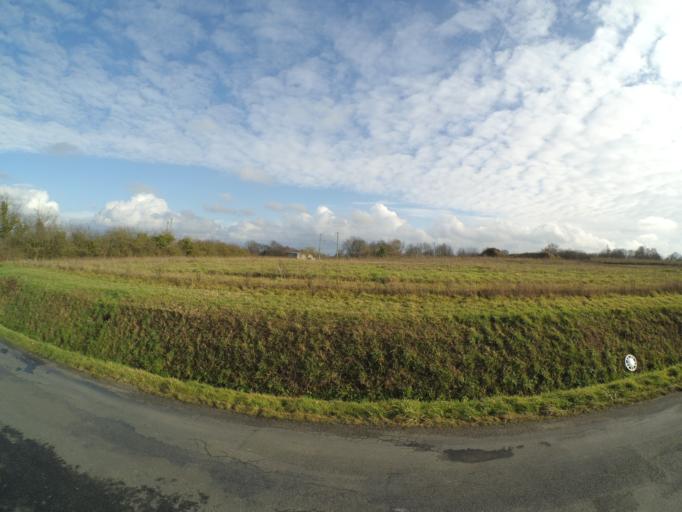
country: FR
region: Pays de la Loire
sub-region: Departement de la Loire-Atlantique
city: Clisson
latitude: 47.0775
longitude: -1.2777
